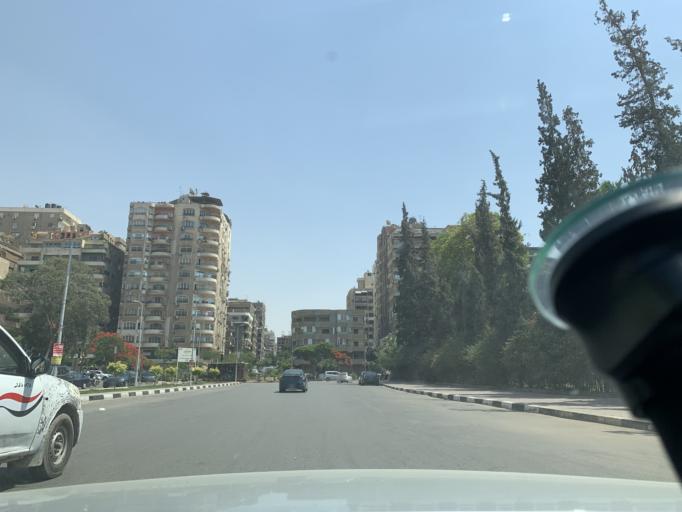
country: EG
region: Muhafazat al Qahirah
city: Cairo
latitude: 30.0618
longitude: 31.3496
